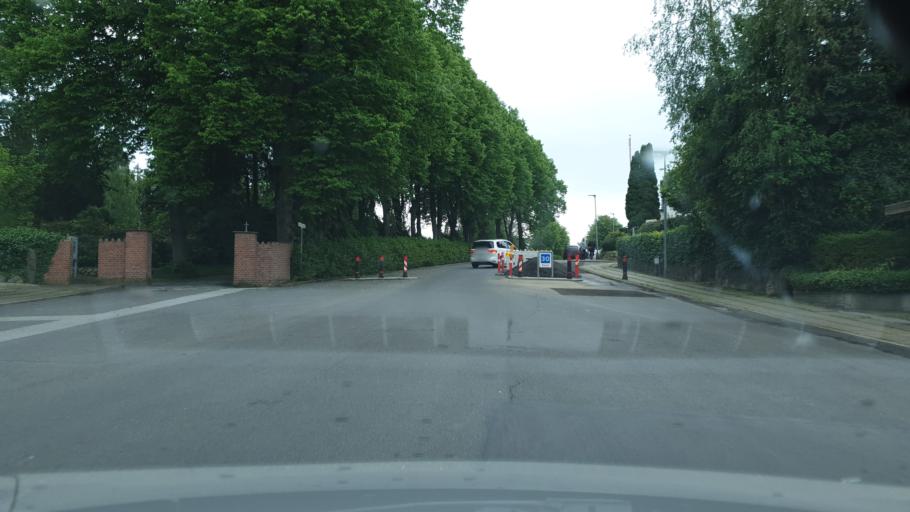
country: DK
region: South Denmark
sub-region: Kolding Kommune
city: Kolding
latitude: 55.4804
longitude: 9.4782
